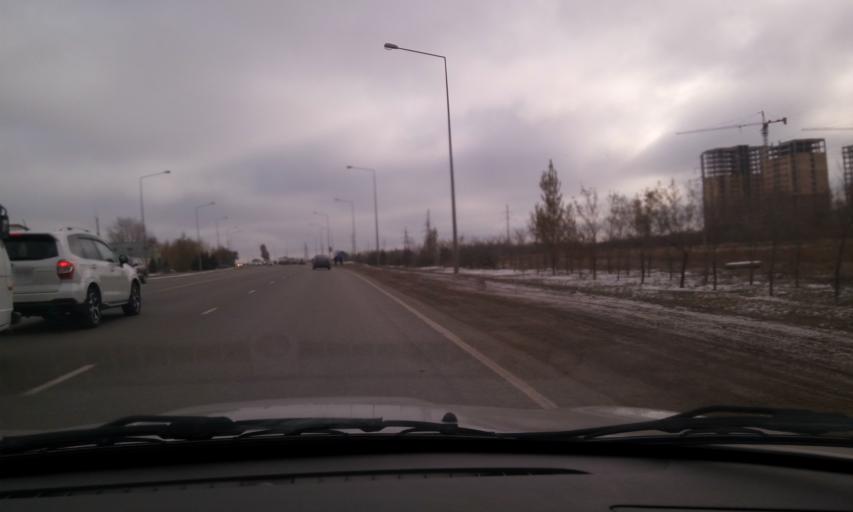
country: KZ
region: Astana Qalasy
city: Astana
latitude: 51.1362
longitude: 71.5363
